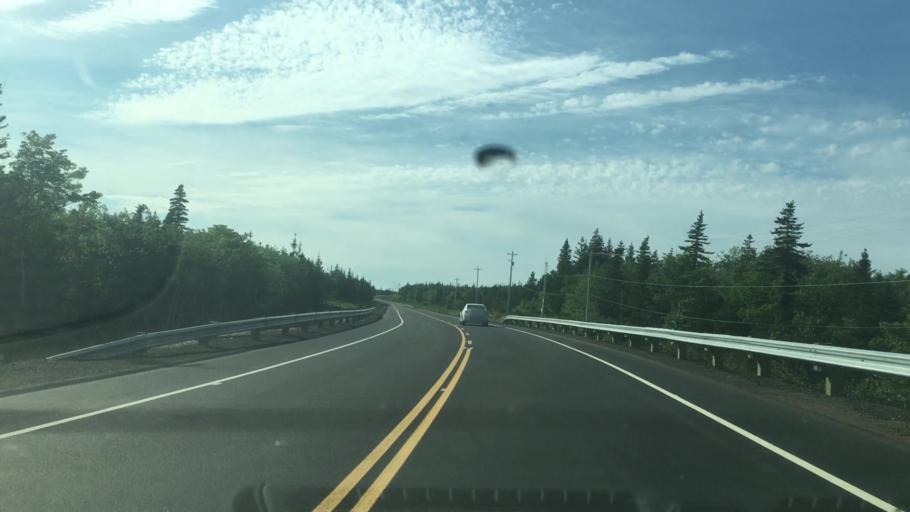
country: CA
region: Nova Scotia
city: Sydney Mines
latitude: 46.8415
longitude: -60.3933
